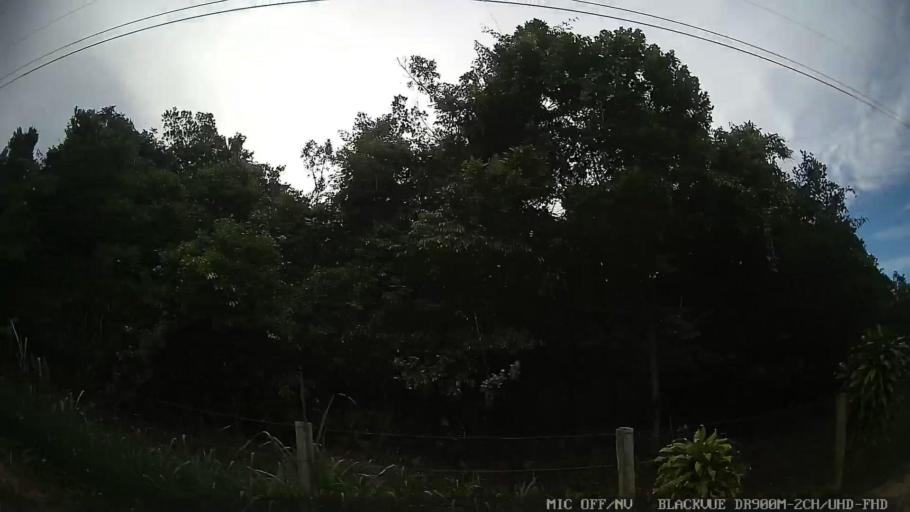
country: BR
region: Sao Paulo
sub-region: Iguape
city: Iguape
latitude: -24.6655
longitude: -47.4339
